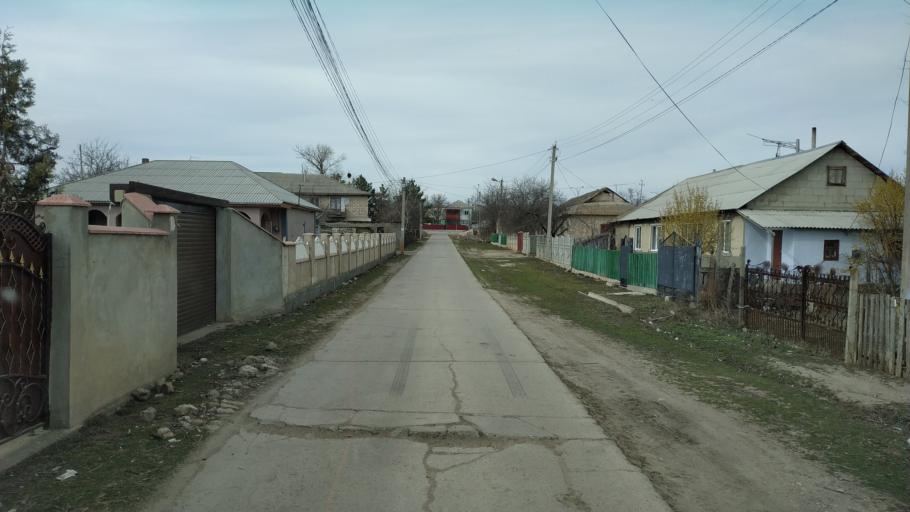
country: MD
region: Hincesti
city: Dancu
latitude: 46.8576
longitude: 28.2511
